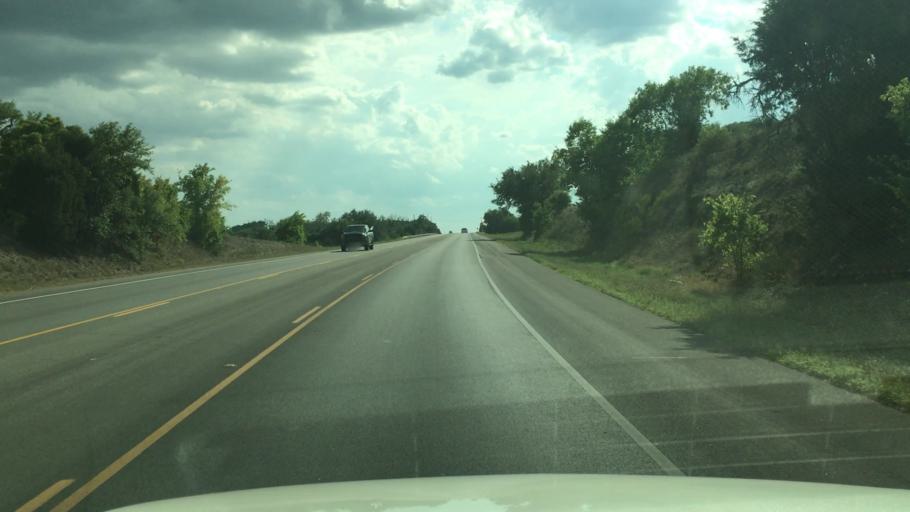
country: US
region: Texas
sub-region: Hays County
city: Dripping Springs
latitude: 30.2012
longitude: -98.1551
